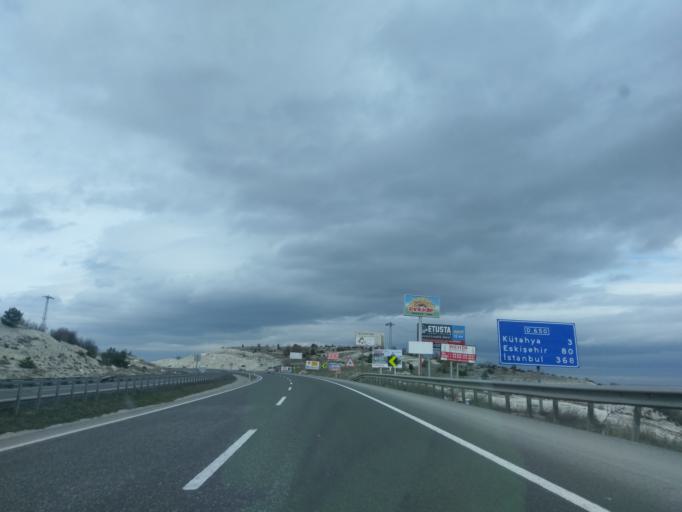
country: TR
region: Kuetahya
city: Kutahya
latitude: 39.3730
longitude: 30.0657
